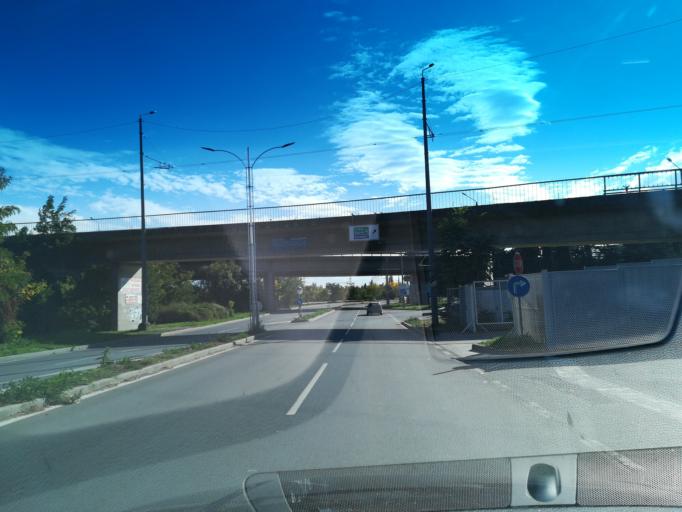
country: BG
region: Stara Zagora
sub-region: Obshtina Stara Zagora
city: Stara Zagora
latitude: 42.4276
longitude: 25.6477
